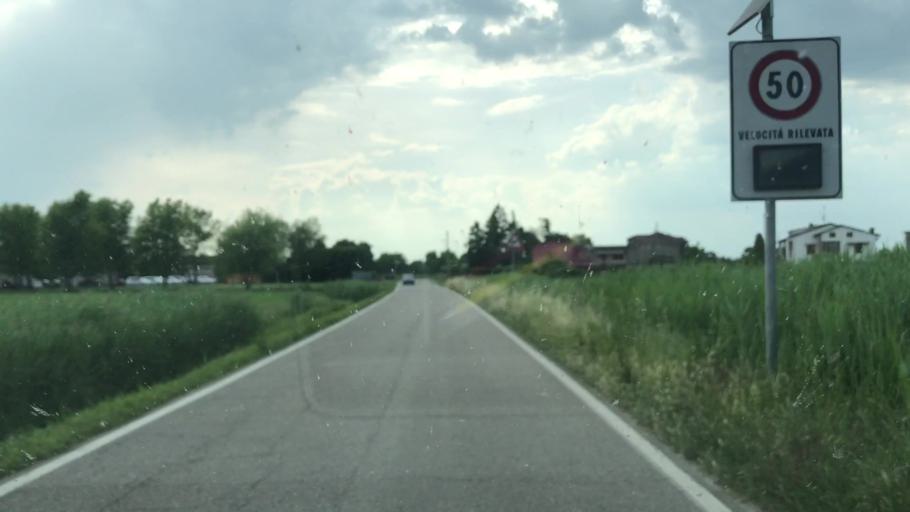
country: IT
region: Lombardy
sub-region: Provincia di Mantova
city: Castel Goffredo
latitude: 45.2938
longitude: 10.4961
